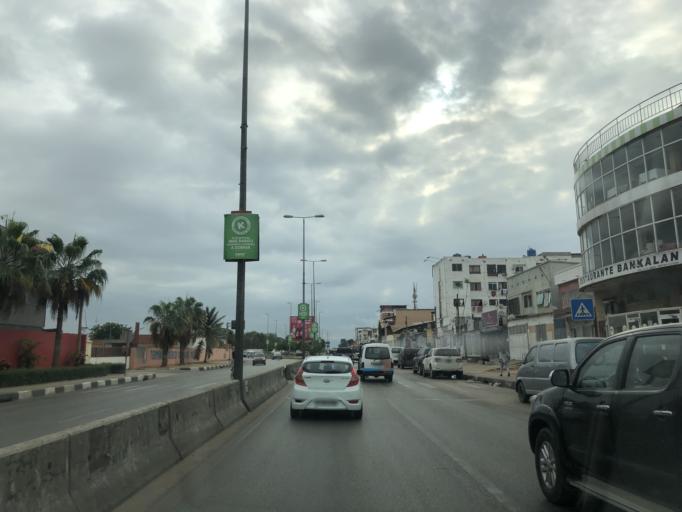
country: AO
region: Luanda
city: Luanda
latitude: -8.8472
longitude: 13.2303
